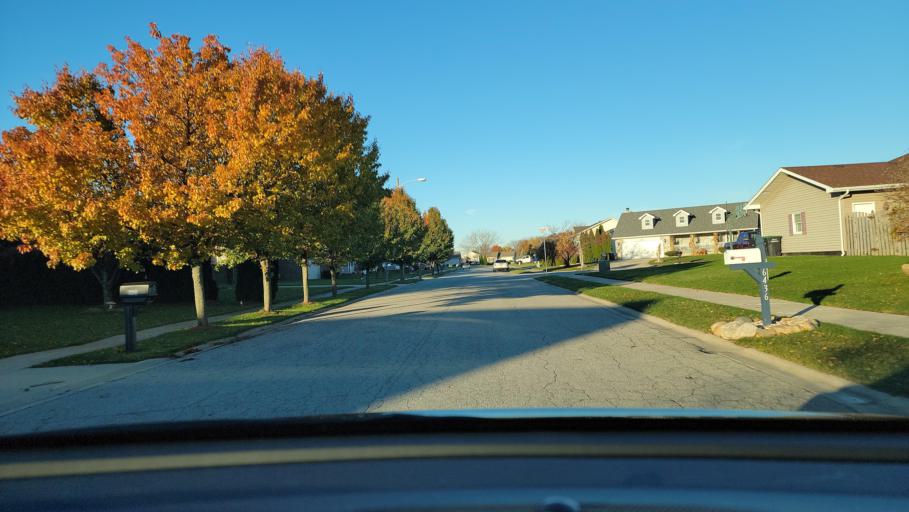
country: US
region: Indiana
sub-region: Porter County
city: Portage
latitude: 41.5619
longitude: -87.1659
